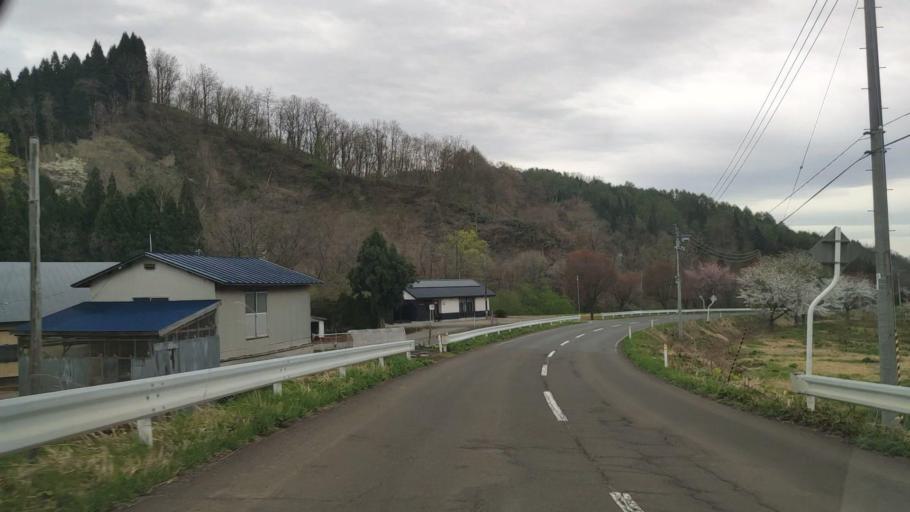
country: JP
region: Akita
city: Hanawa
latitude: 40.3595
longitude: 140.7852
